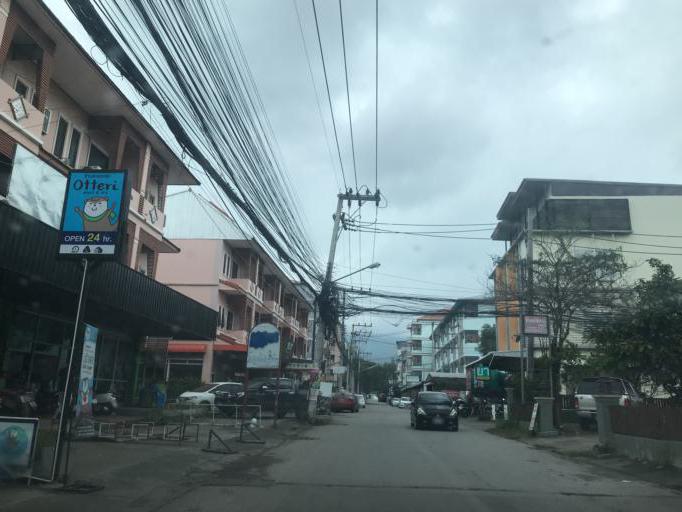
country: TH
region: Chiang Mai
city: Chiang Mai
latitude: 18.8037
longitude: 98.9746
